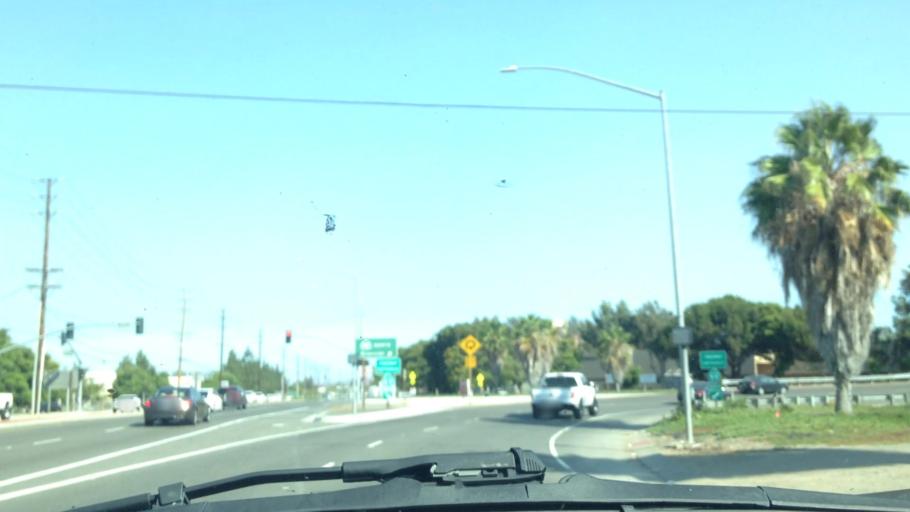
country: US
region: California
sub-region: Orange County
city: Irvine
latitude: 33.6964
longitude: -117.8621
